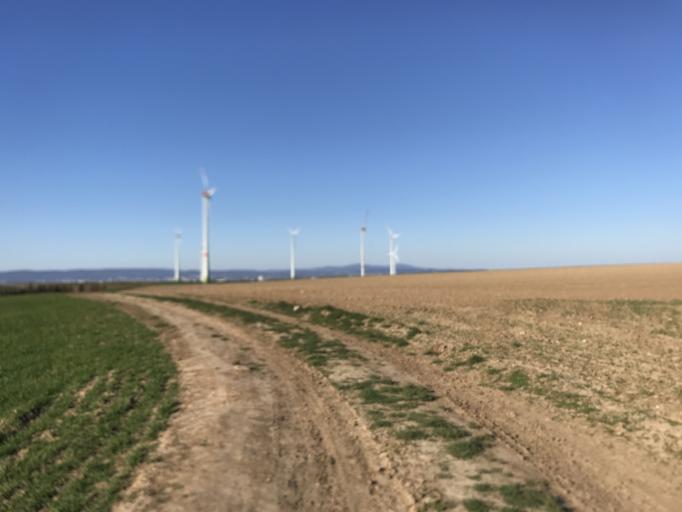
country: DE
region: Rheinland-Pfalz
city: Klein-Winternheim
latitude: 49.9274
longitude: 8.2349
